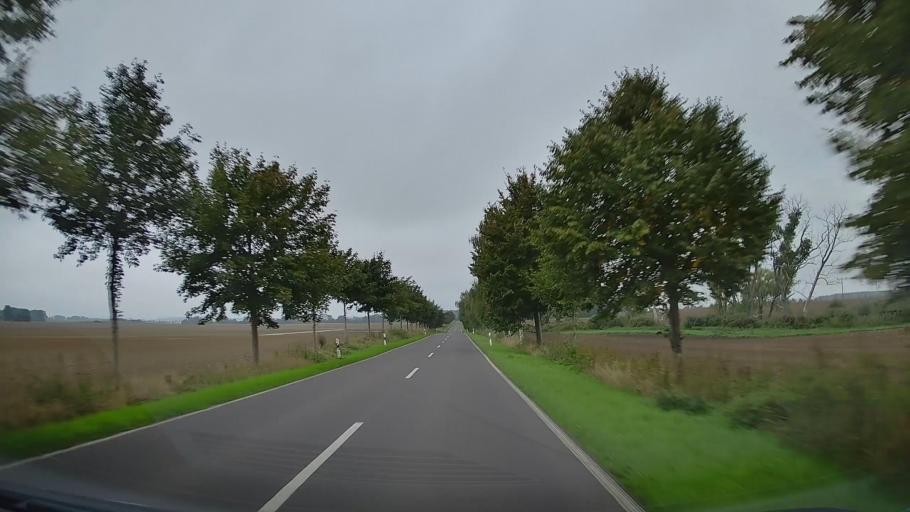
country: DE
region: Mecklenburg-Vorpommern
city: Guestrow
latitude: 53.7959
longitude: 12.0970
